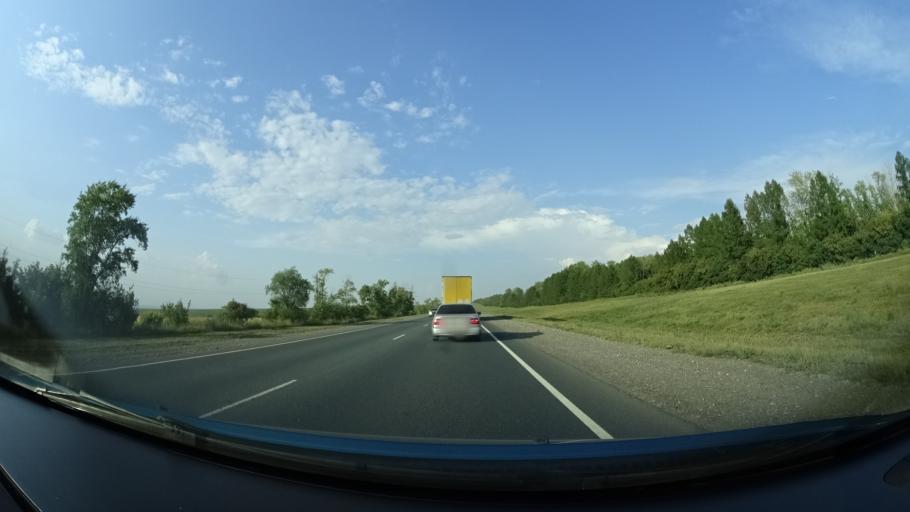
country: RU
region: Samara
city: Krasnyy Yar
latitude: 53.6538
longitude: 50.7459
